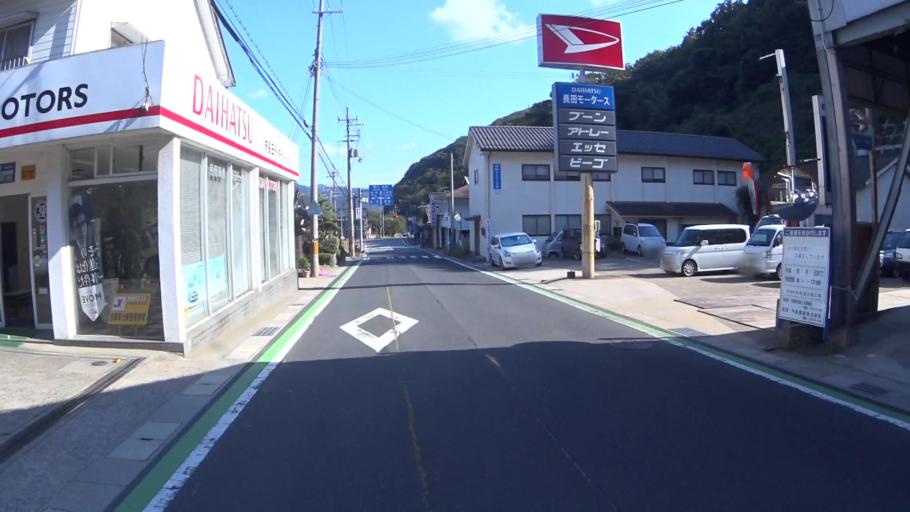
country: JP
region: Kyoto
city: Miyazu
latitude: 35.7321
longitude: 135.0947
